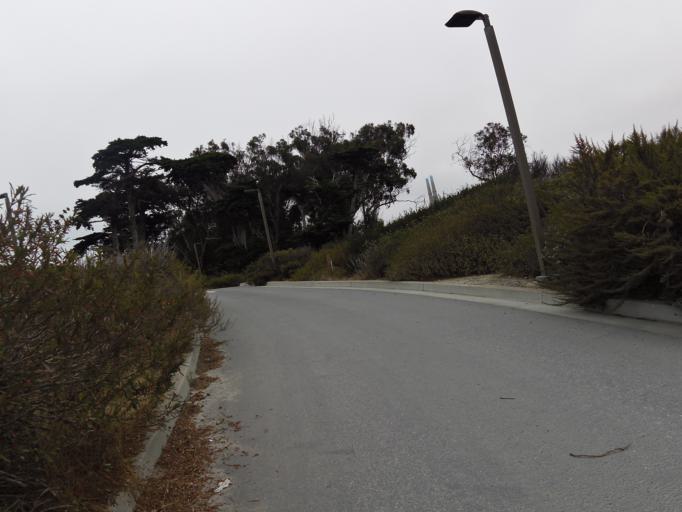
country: US
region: California
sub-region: Monterey County
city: Castroville
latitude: 36.7941
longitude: -121.7866
